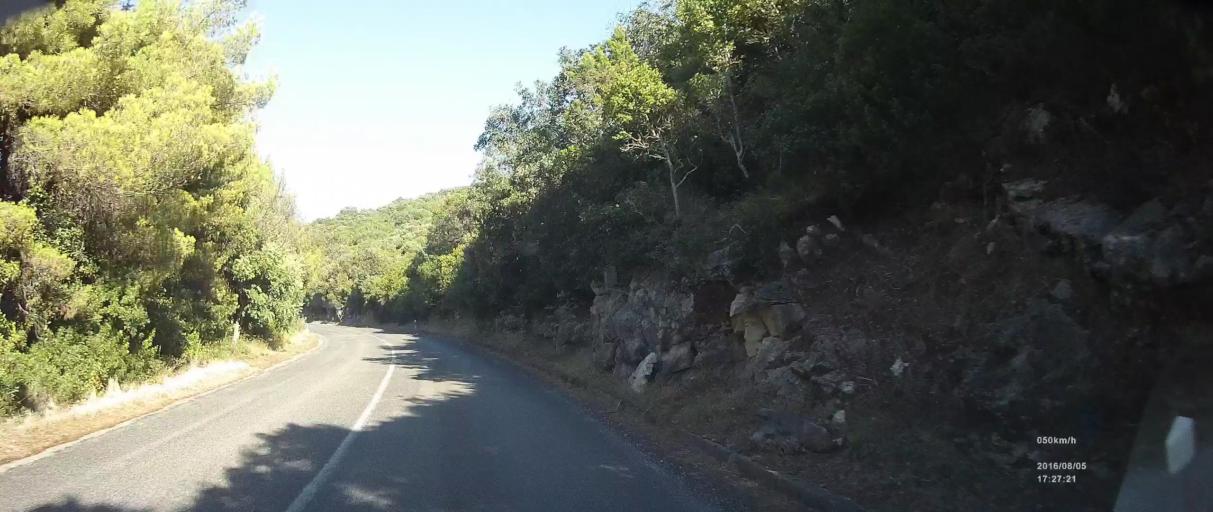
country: HR
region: Dubrovacko-Neretvanska
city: Blato
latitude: 42.7861
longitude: 17.3953
